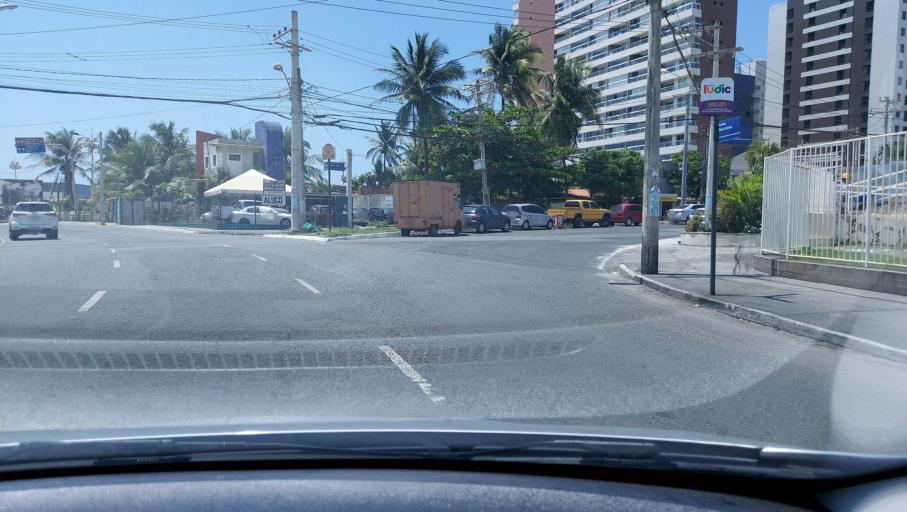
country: BR
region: Bahia
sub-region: Salvador
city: Salvador
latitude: -12.9852
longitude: -38.4369
